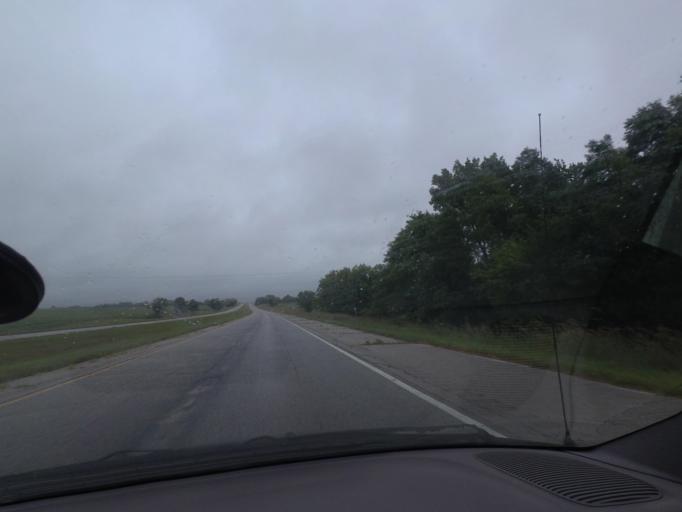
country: US
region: Illinois
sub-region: Pike County
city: Pittsfield
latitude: 39.6698
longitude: -90.8199
